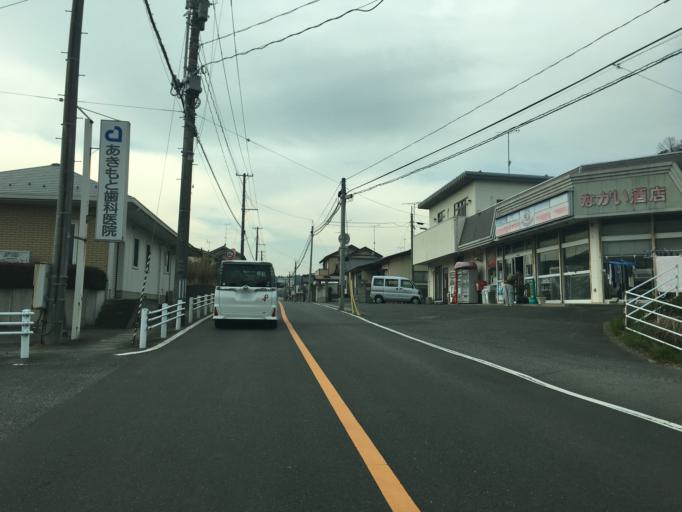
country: JP
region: Fukushima
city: Iwaki
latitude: 36.9844
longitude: 140.8910
